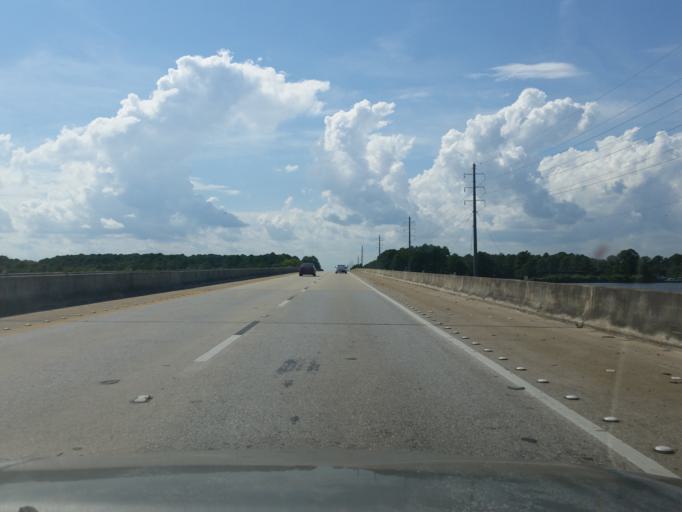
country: US
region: Alabama
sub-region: Baldwin County
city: Spanish Fort
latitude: 30.6678
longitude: -87.9234
